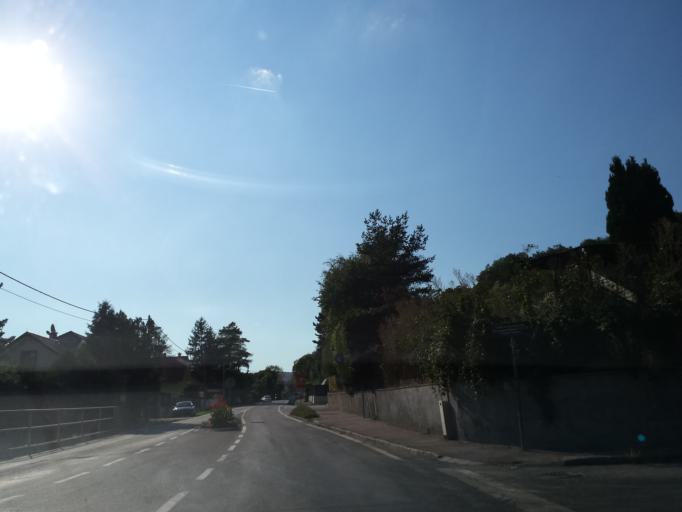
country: AT
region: Lower Austria
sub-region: Politischer Bezirk Modling
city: Kaltenleutgeben
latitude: 48.1372
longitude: 16.2206
